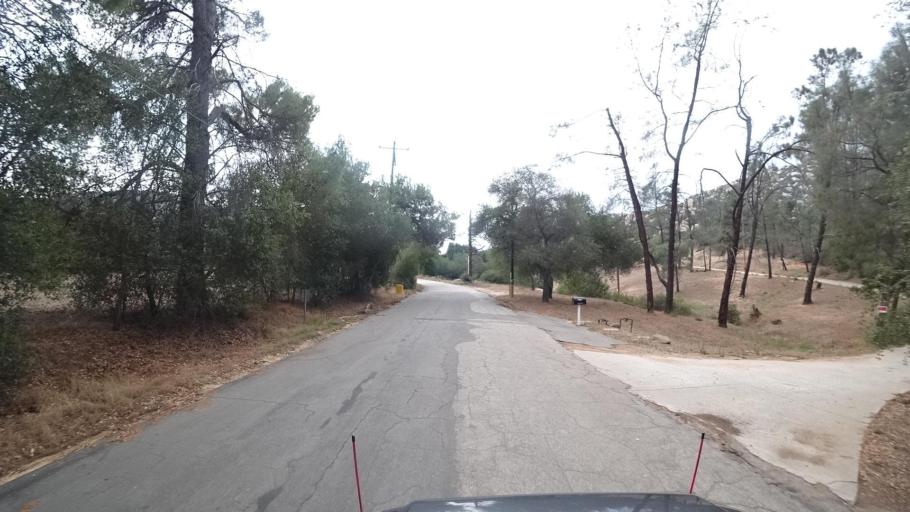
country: US
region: California
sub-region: San Diego County
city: San Pasqual
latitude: 33.0059
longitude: -116.9575
